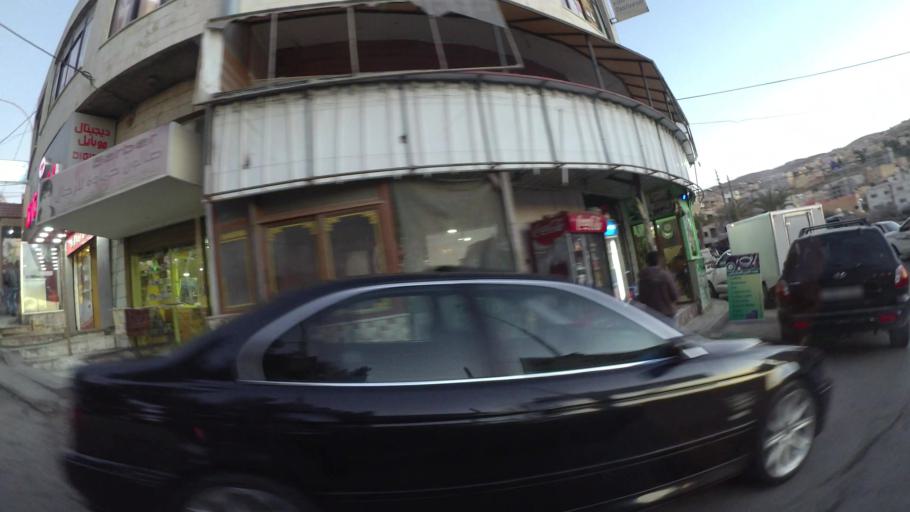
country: JO
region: Ma'an
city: Petra
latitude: 30.3220
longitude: 35.4786
